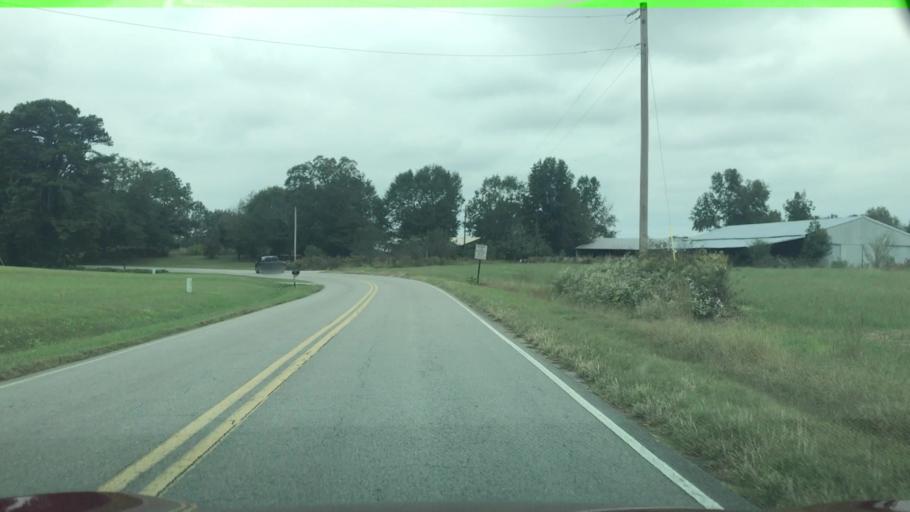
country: US
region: Alabama
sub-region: Cullman County
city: Good Hope
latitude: 34.0965
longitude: -87.0481
